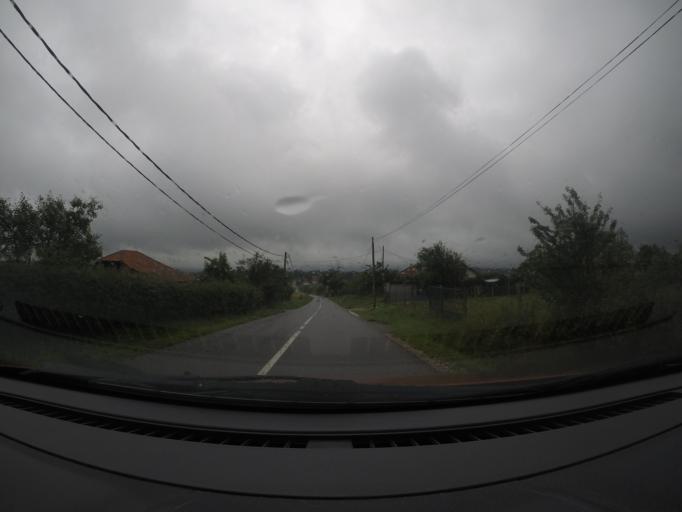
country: RS
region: Central Serbia
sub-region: Belgrade
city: Sopot
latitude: 44.5282
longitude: 20.5404
